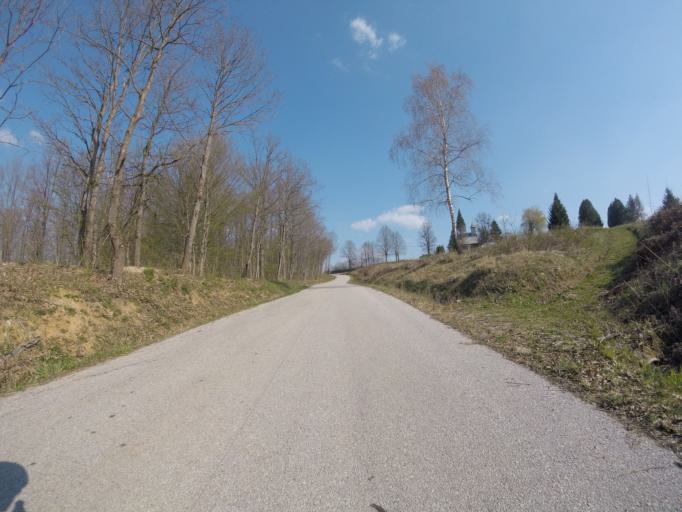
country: HR
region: Sisacko-Moslavacka
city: Gvozd
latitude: 45.5135
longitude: 15.9304
